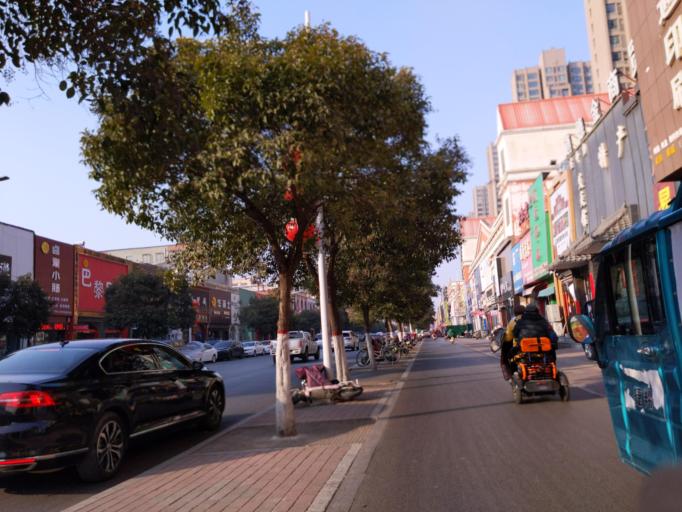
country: CN
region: Henan Sheng
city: Puyang
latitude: 35.7731
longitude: 115.0328
